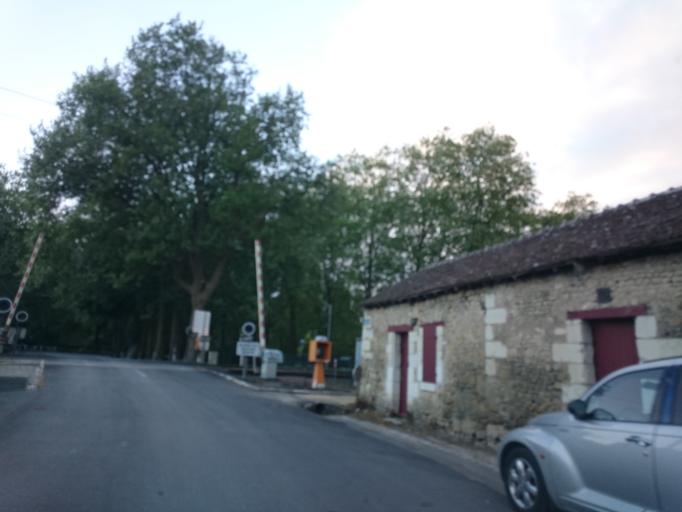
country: FR
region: Centre
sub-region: Departement d'Indre-et-Loire
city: Civray-de-Touraine
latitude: 47.3308
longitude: 1.0666
